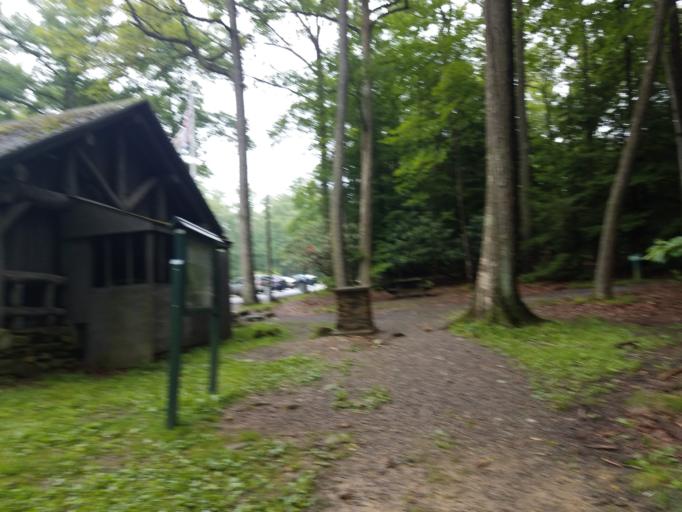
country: US
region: West Virginia
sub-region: Monongalia County
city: Cheat Lake
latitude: 39.6380
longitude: -79.8158
